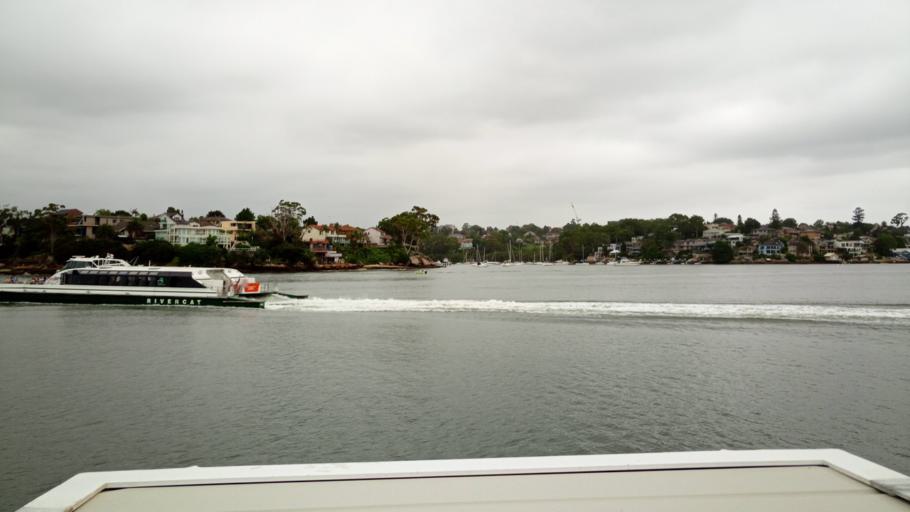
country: AU
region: New South Wales
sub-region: Canada Bay
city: Concord
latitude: -33.8393
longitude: 151.1141
